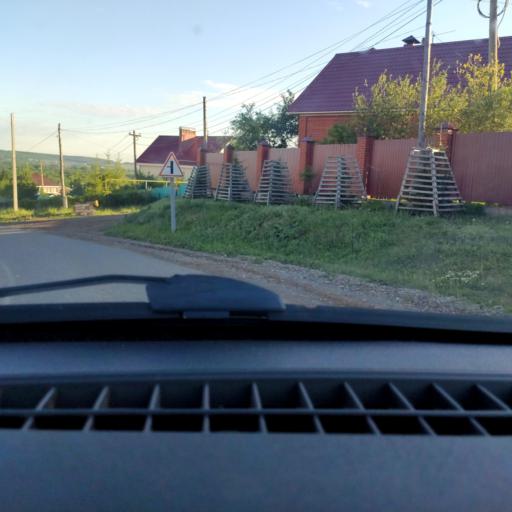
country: RU
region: Bashkortostan
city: Avdon
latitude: 54.6264
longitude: 55.6875
